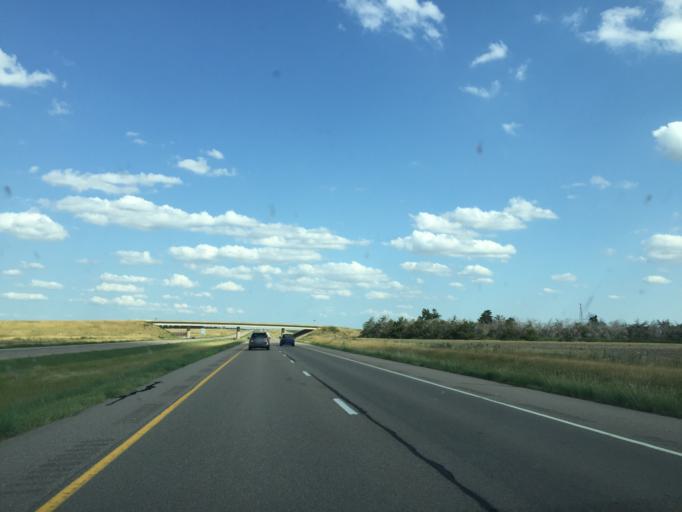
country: US
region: Kansas
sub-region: Gove County
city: Gove
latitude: 39.0504
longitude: -100.2258
